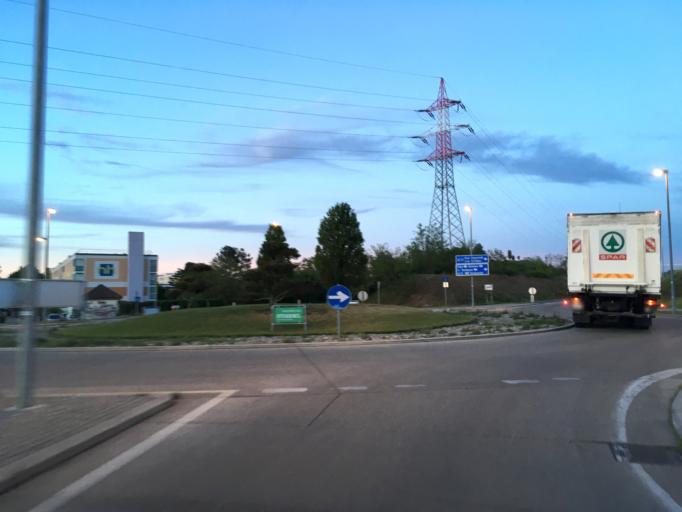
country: AT
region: Lower Austria
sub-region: Politischer Bezirk Wien-Umgebung
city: Schwechat
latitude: 48.1223
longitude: 16.4706
